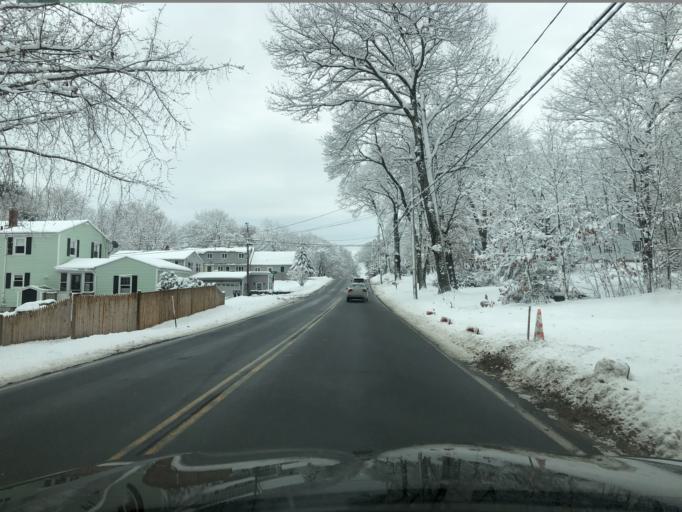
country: US
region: New Hampshire
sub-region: Strafford County
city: Somersworth
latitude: 43.2356
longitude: -70.8630
